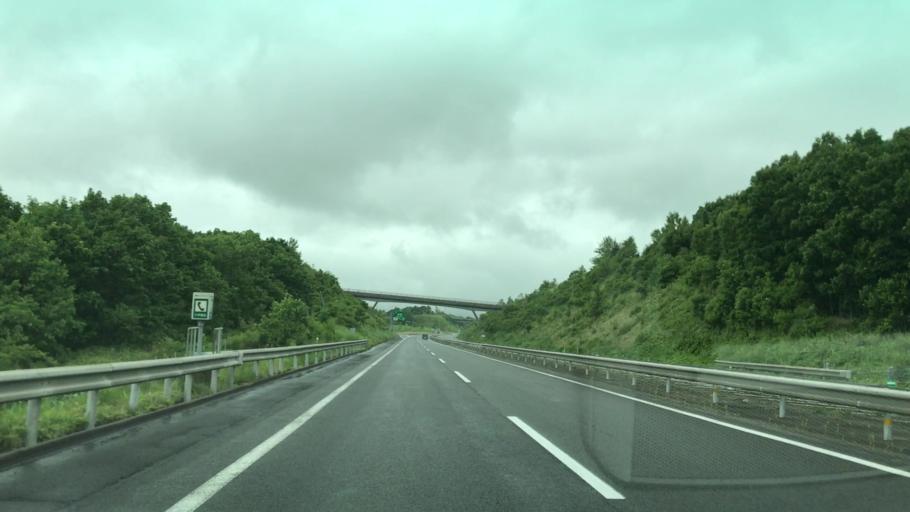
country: JP
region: Hokkaido
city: Muroran
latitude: 42.3859
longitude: 140.9787
